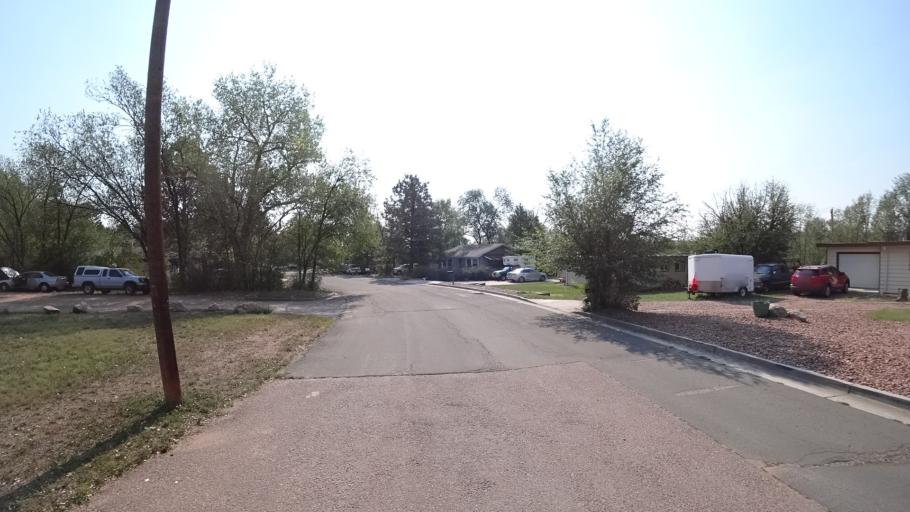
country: US
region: Colorado
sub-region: El Paso County
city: Colorado Springs
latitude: 38.8107
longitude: -104.8366
